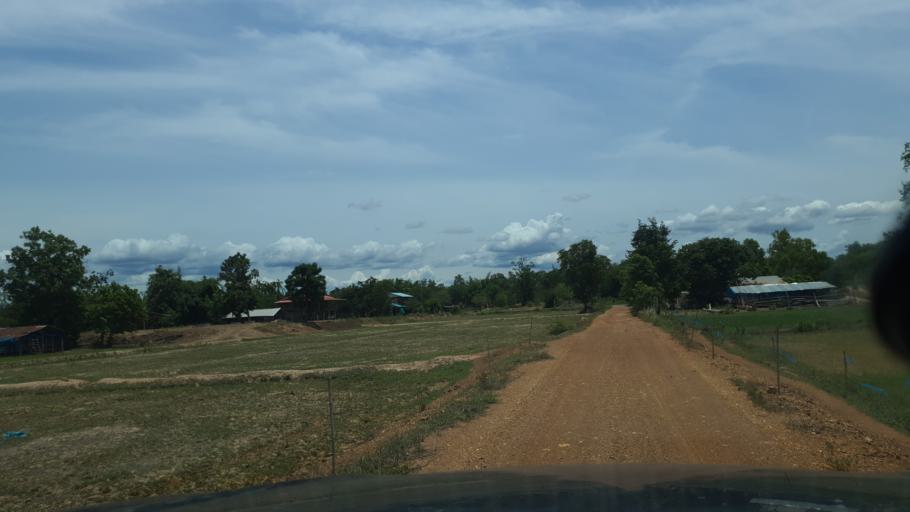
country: TH
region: Sukhothai
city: Ban Na
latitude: 17.1492
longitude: 99.6686
